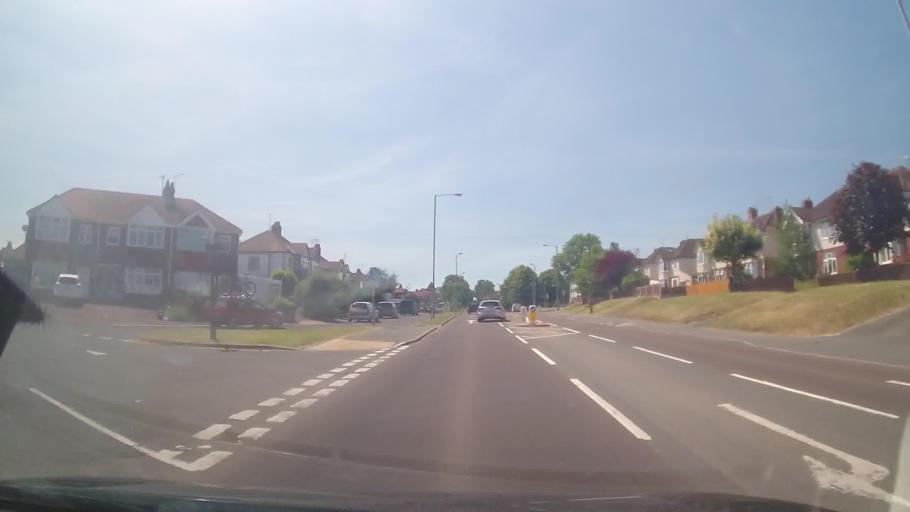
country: GB
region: England
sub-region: Herefordshire
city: Hereford
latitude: 52.0411
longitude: -2.7206
